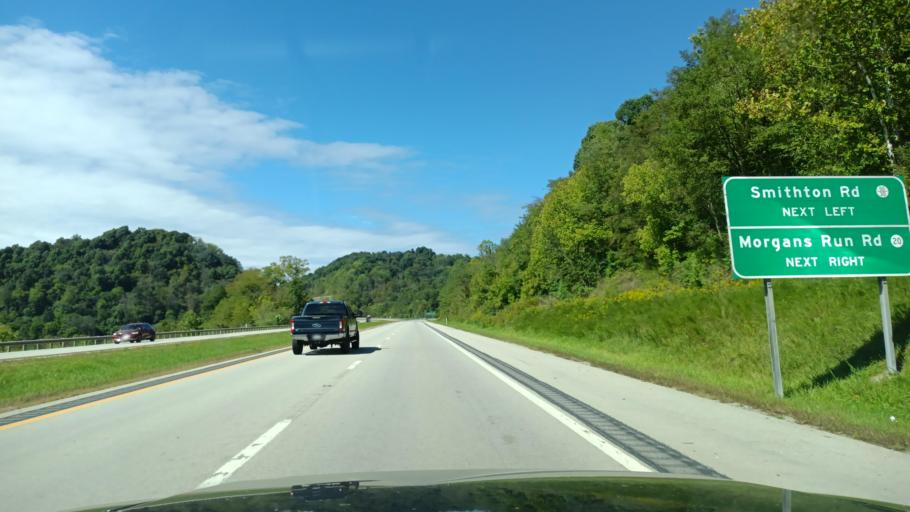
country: US
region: West Virginia
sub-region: Doddridge County
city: West Union
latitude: 39.2805
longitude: -80.6908
